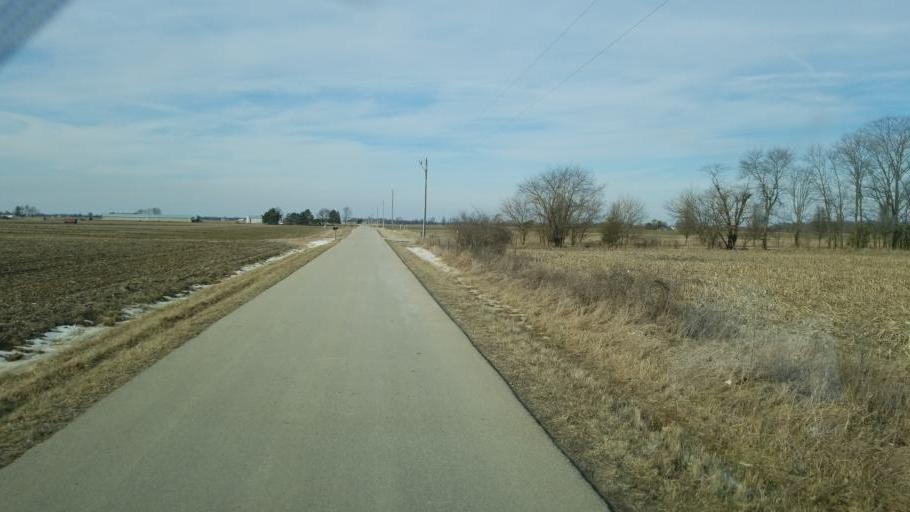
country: US
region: Ohio
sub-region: Marion County
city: Prospect
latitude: 40.4096
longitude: -83.2222
